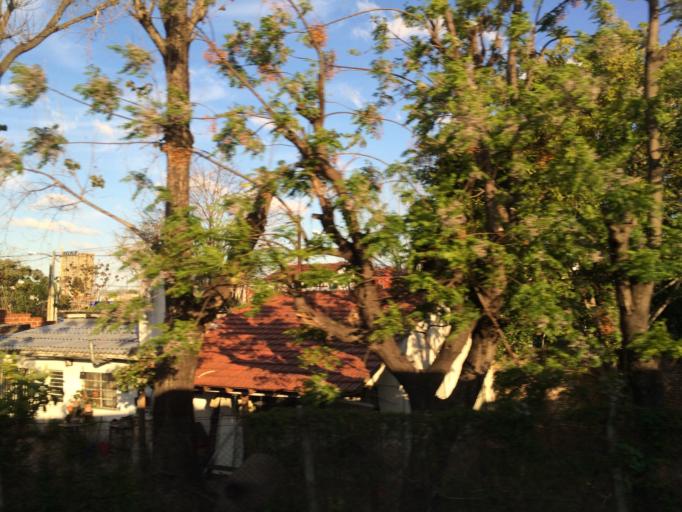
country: AR
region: Buenos Aires
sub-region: Partido de Lanus
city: Lanus
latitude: -34.6982
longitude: -58.3871
